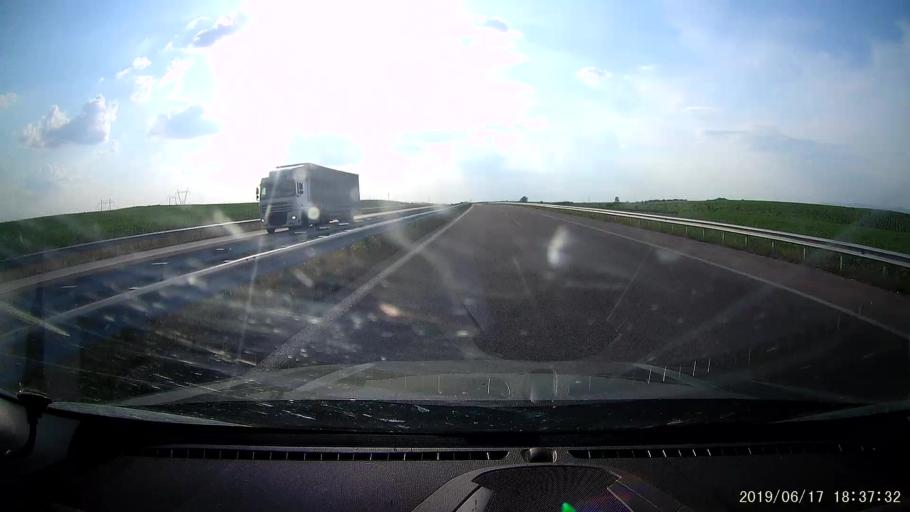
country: BG
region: Stara Zagora
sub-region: Obshtina Chirpan
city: Chirpan
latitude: 42.1314
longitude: 25.3584
